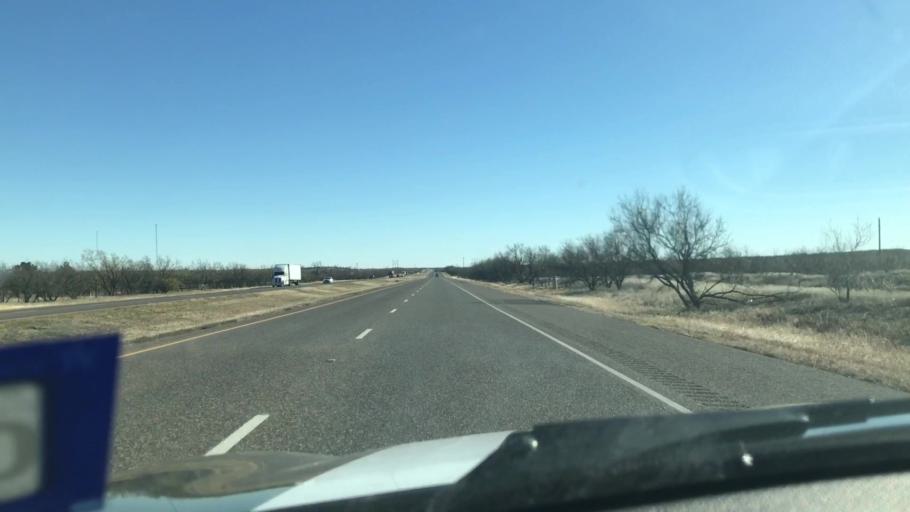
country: US
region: Texas
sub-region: Scurry County
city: Snyder
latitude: 32.8294
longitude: -100.9846
